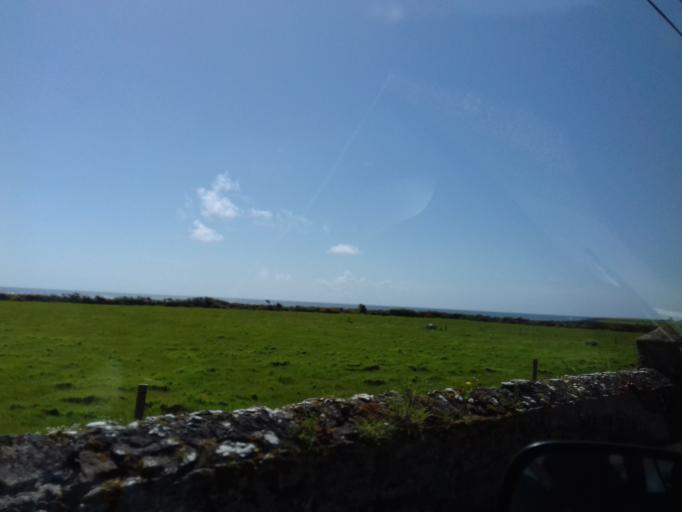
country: IE
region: Munster
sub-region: Waterford
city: Dunmore East
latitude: 52.1543
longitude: -6.8977
